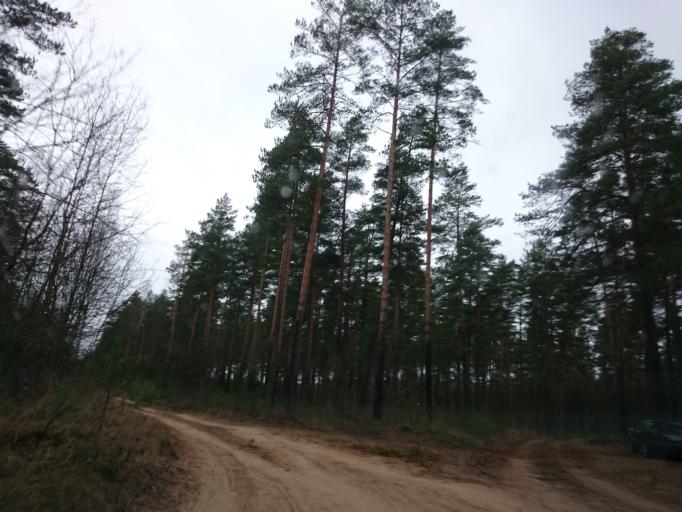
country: LV
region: Riga
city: Bergi
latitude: 57.0171
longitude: 24.3510
